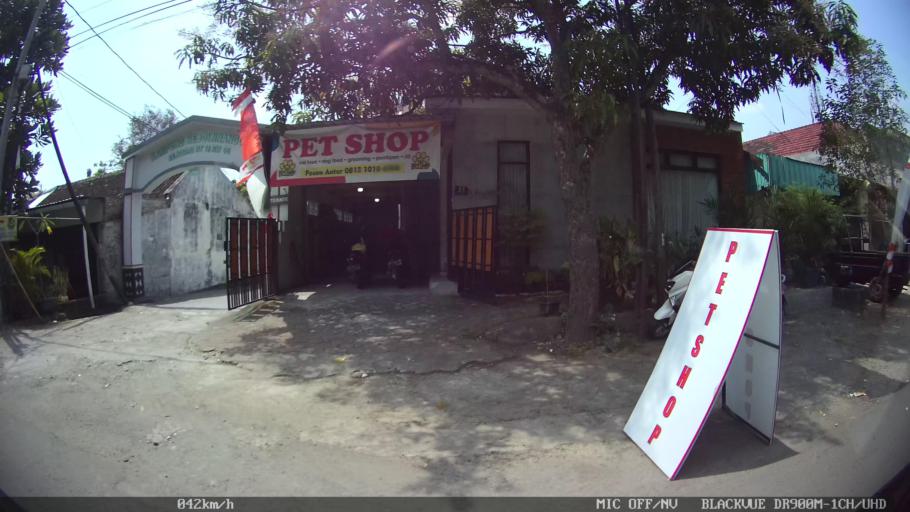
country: ID
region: Daerah Istimewa Yogyakarta
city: Yogyakarta
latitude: -7.8057
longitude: 110.3983
